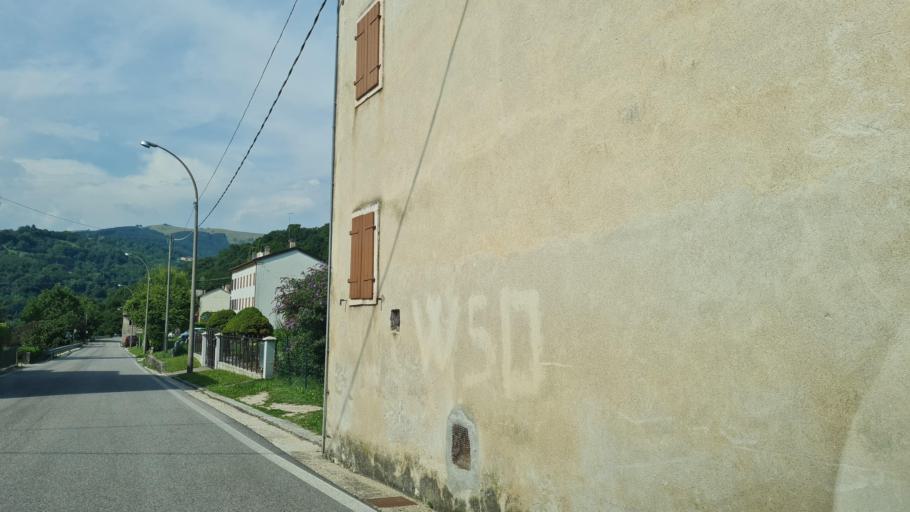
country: IT
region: Veneto
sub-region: Provincia di Vicenza
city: Conco
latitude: 45.7847
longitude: 11.6297
